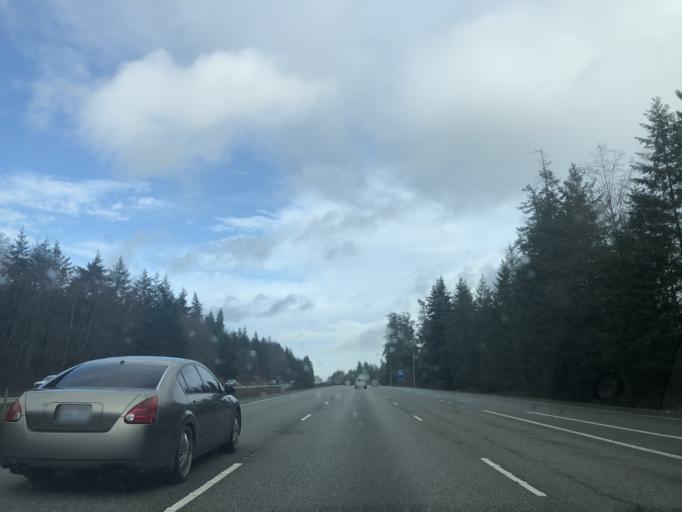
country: US
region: Washington
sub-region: Kitsap County
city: Silverdale
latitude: 47.6818
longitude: -122.6899
